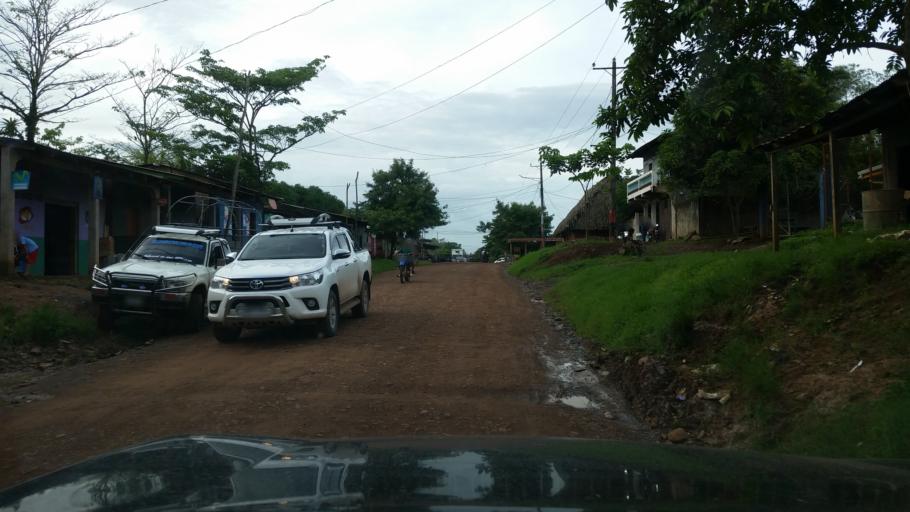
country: NI
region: Matagalpa
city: Rio Blanco
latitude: 13.1795
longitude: -84.9514
